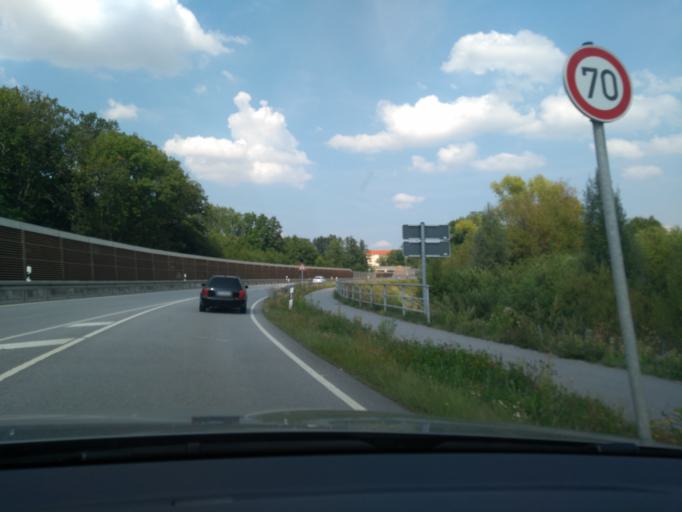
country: DE
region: Saxony
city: Bautzen
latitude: 51.1738
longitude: 14.4079
